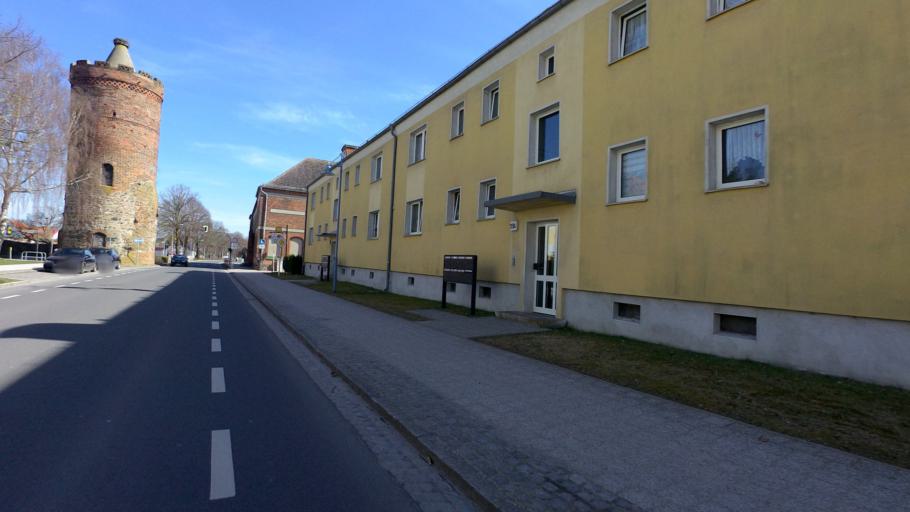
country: DE
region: Brandenburg
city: Muncheberg
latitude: 52.5017
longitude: 14.1443
